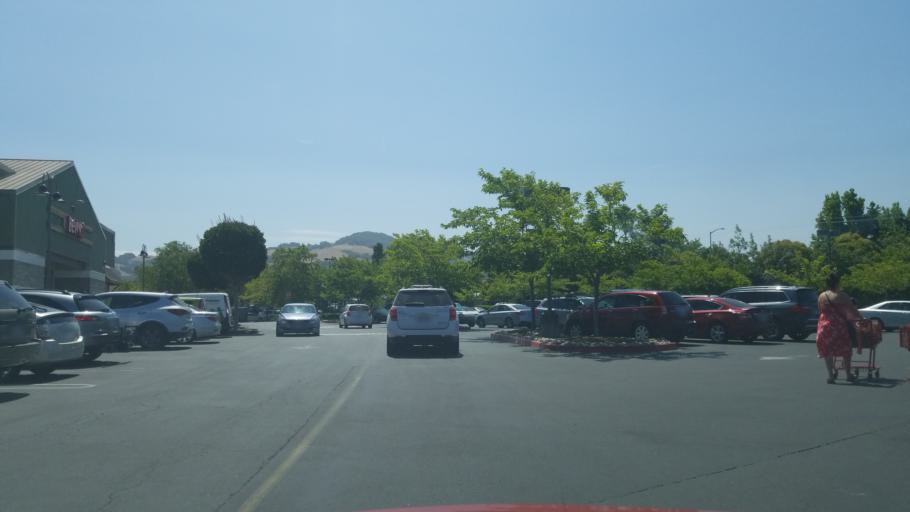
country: US
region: California
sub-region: Sonoma County
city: Roseland
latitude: 38.4172
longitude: -122.7121
